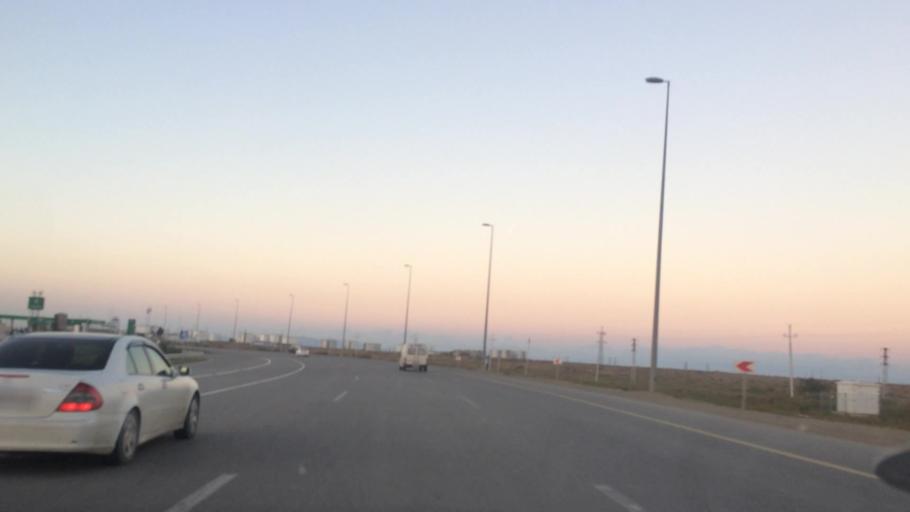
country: AZ
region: Baki
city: Qobustan
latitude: 39.9920
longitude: 49.4310
